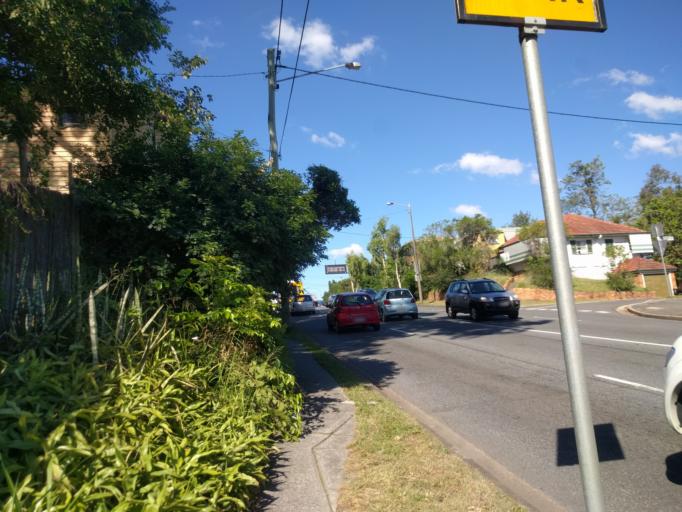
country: AU
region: Queensland
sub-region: Brisbane
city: Milton
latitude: -27.4732
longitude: 152.9963
